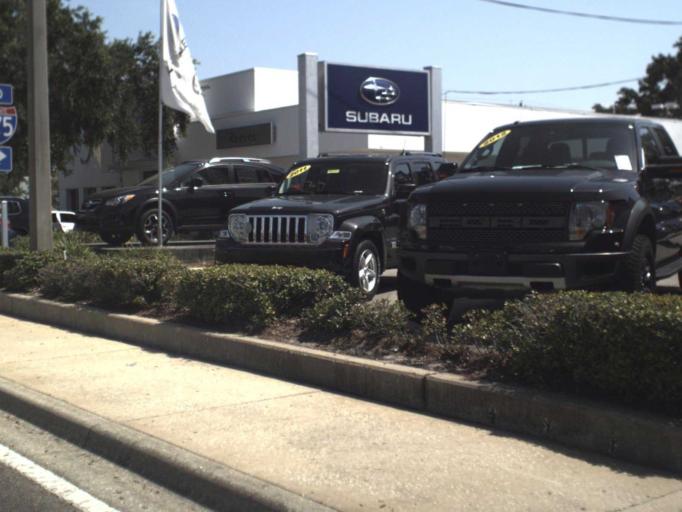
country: US
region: Florida
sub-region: Hillsborough County
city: Lake Magdalene
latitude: 28.0531
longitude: -82.4593
